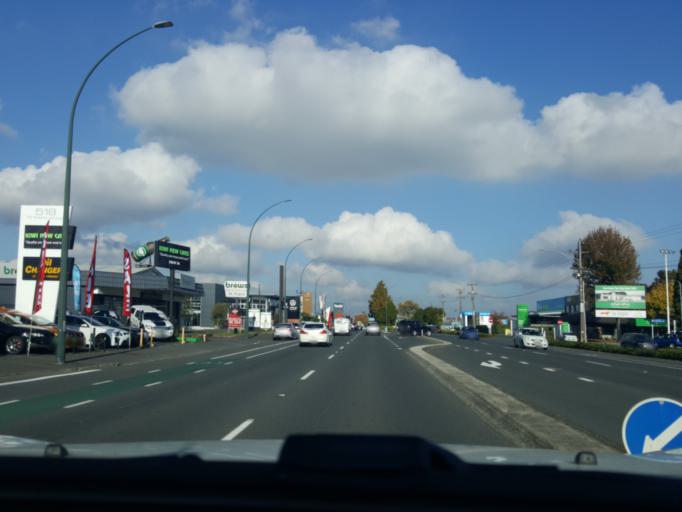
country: NZ
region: Waikato
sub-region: Hamilton City
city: Hamilton
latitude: -37.7606
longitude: 175.2490
